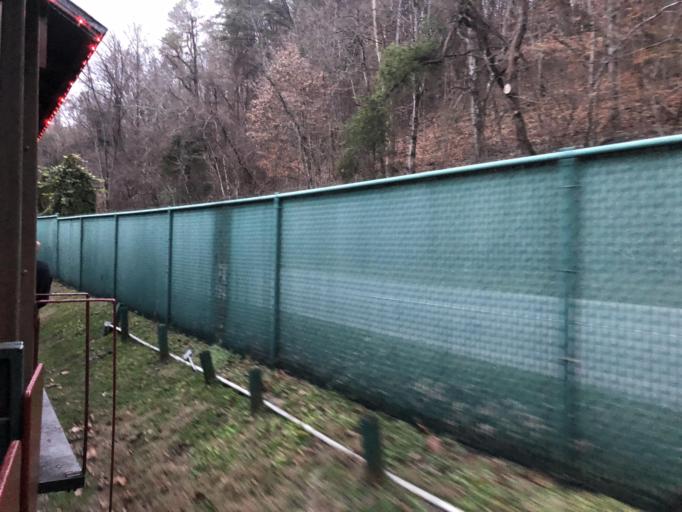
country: US
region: Tennessee
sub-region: Sevier County
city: Pigeon Forge
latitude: 35.7925
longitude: -83.5358
